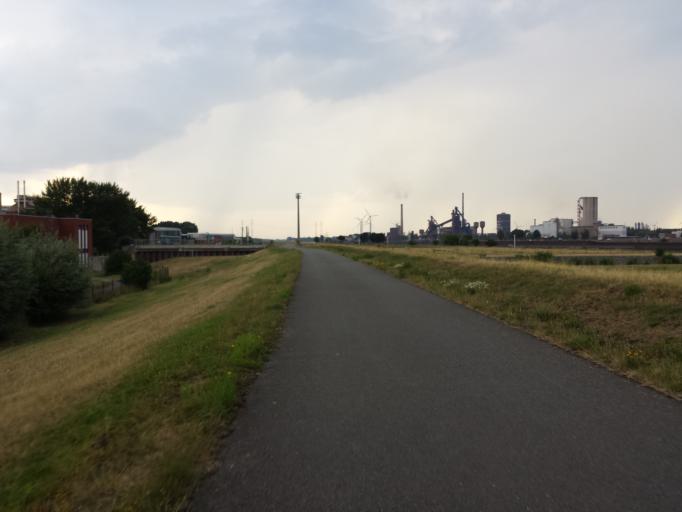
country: DE
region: Lower Saxony
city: Ritterhude
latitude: 53.1150
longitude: 8.7161
